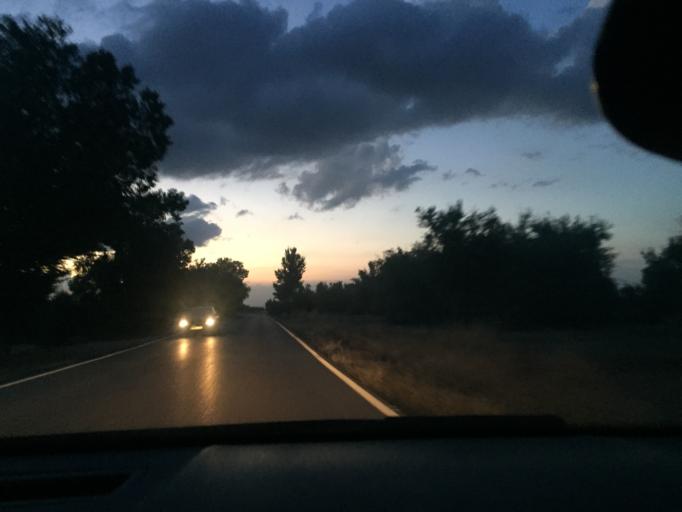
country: ES
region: Andalusia
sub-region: Provincia de Jaen
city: Mancha Real
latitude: 37.7908
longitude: -3.6273
